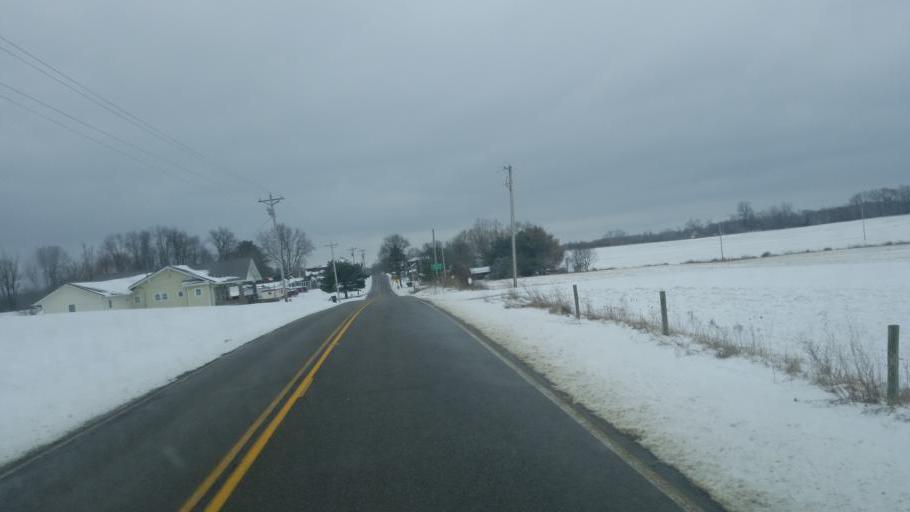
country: US
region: Ohio
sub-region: Knox County
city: Oak Hill
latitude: 40.4214
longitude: -82.1379
